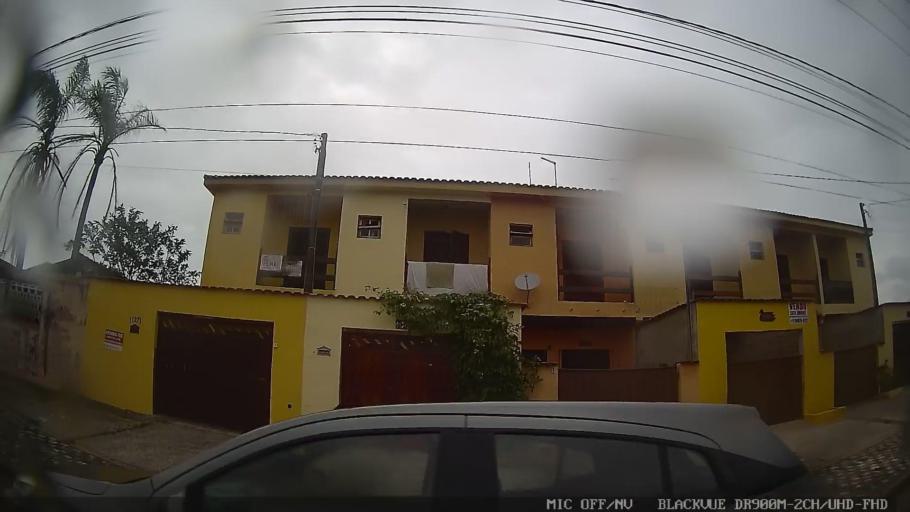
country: BR
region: Sao Paulo
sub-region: Mongagua
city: Mongagua
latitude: -24.1369
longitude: -46.7022
